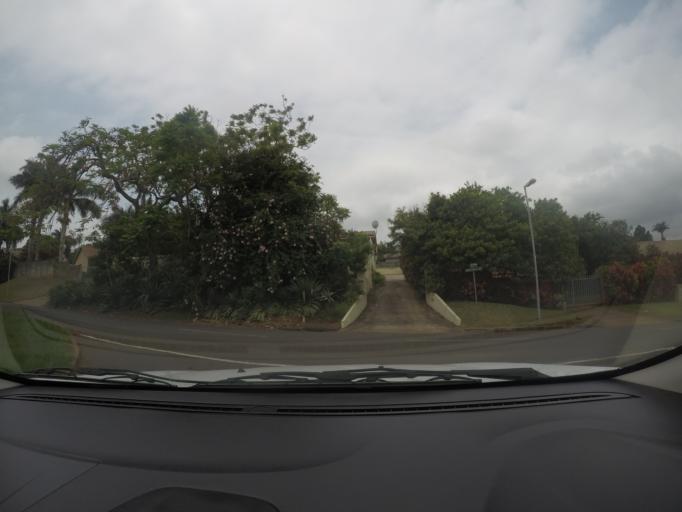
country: ZA
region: KwaZulu-Natal
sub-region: uThungulu District Municipality
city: Empangeni
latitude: -28.7535
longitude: 31.8923
